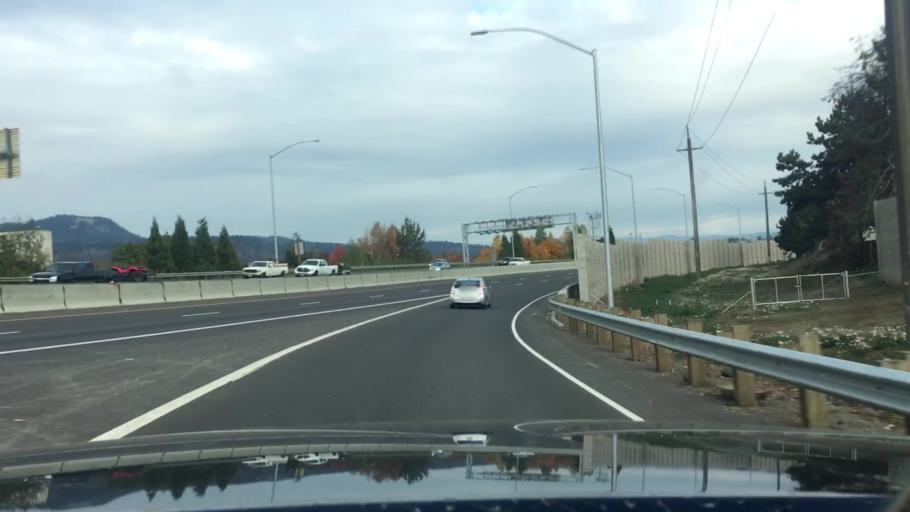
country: US
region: Oregon
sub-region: Lane County
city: Eugene
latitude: 44.0875
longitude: -123.0647
